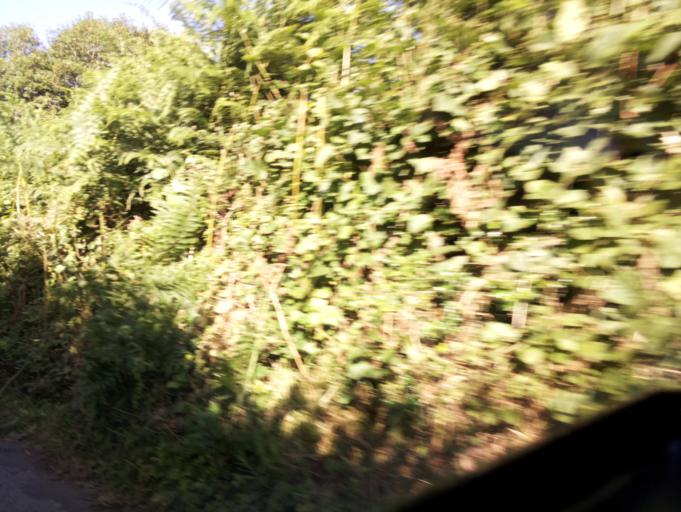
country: GB
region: Wales
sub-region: Monmouthshire
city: Tintern
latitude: 51.6860
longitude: -2.7358
